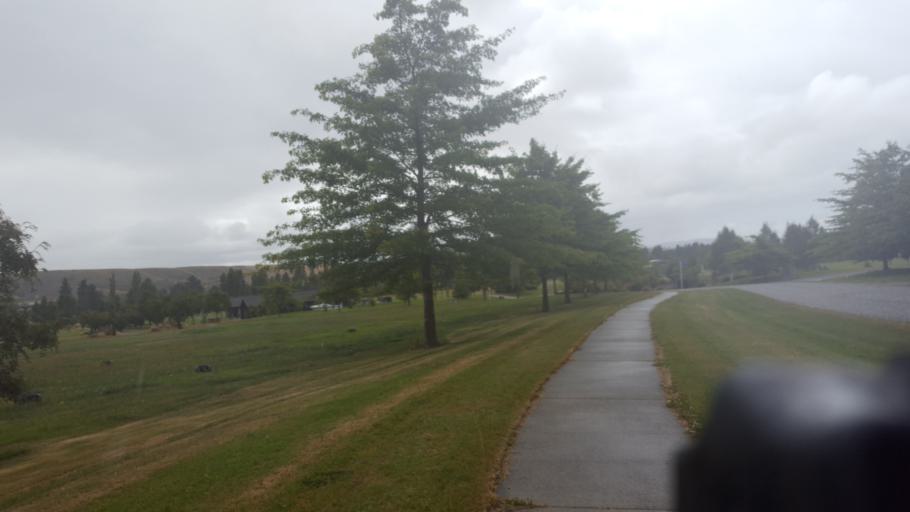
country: NZ
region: Otago
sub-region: Queenstown-Lakes District
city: Wanaka
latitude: -45.1964
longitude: 169.3155
